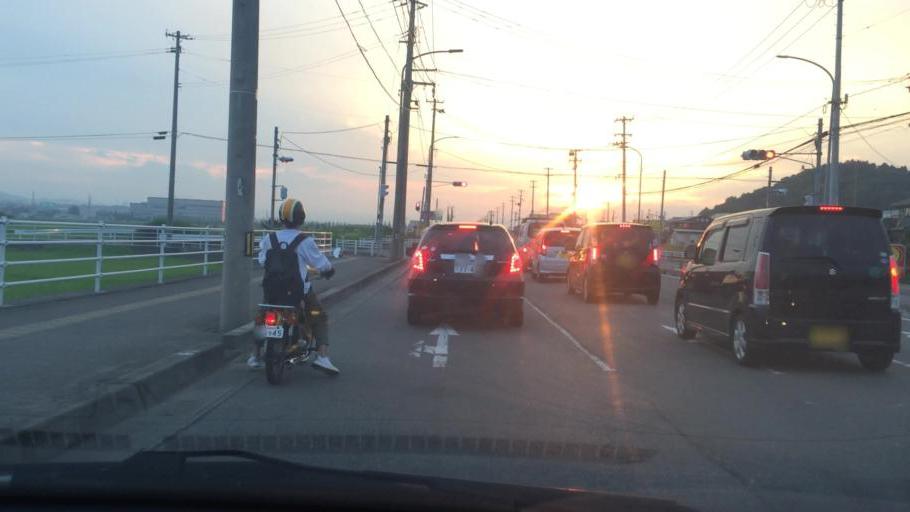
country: JP
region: Miyagi
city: Rifu
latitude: 38.3079
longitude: 140.9361
